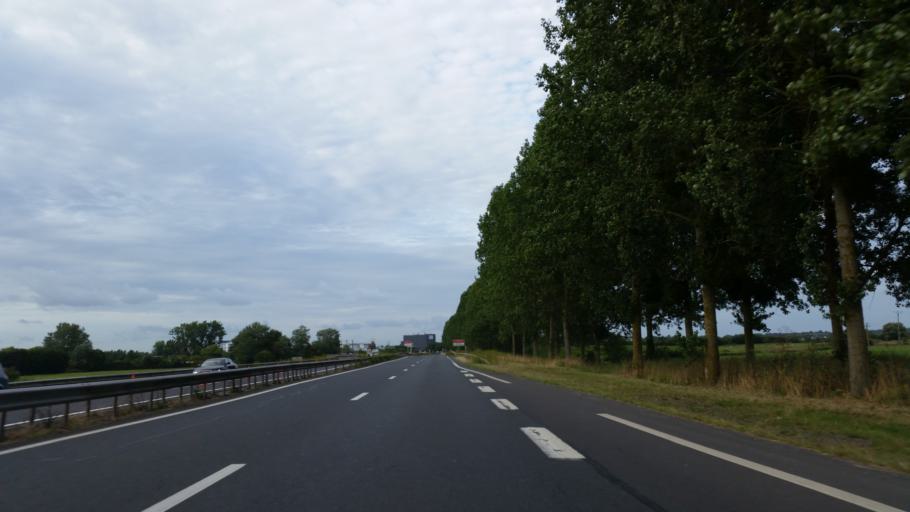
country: FR
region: Lower Normandy
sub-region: Departement du Calvados
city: Isigny-sur-Mer
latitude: 49.3138
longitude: -1.0958
